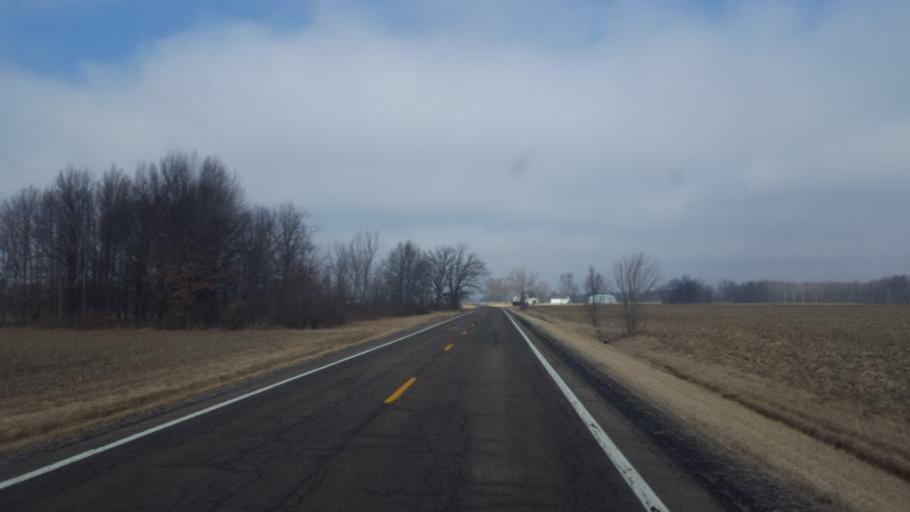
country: US
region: Ohio
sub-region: Crawford County
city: Galion
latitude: 40.7008
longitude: -82.8688
